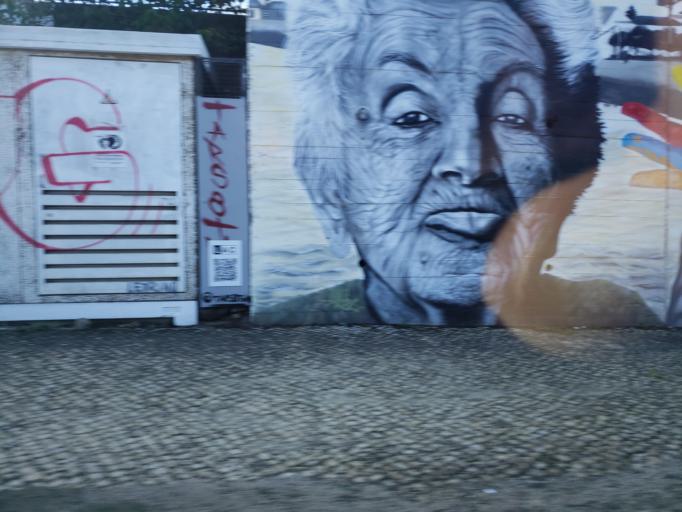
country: PT
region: Faro
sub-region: Portimao
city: Portimao
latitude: 37.1511
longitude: -8.5527
